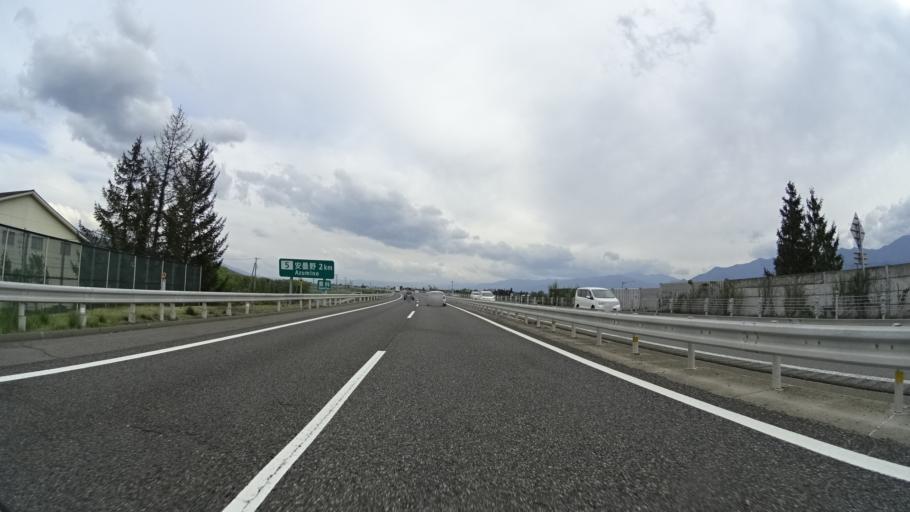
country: JP
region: Nagano
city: Toyoshina
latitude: 36.3162
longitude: 137.9204
